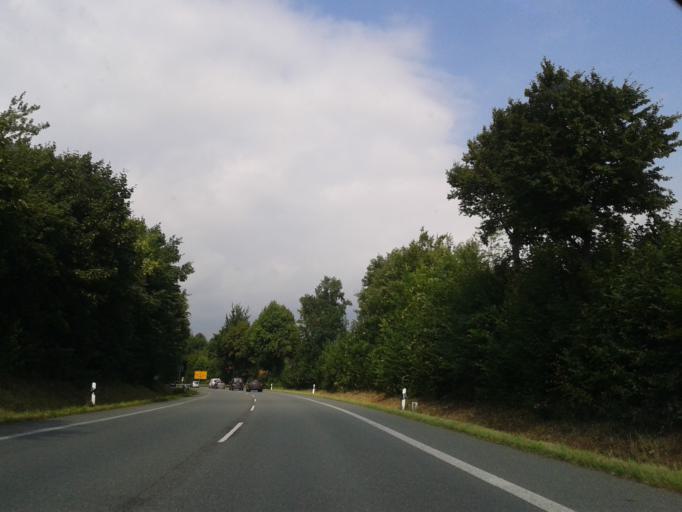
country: DE
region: North Rhine-Westphalia
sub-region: Regierungsbezirk Detmold
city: Dorentrup
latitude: 51.9846
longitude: 9.0044
